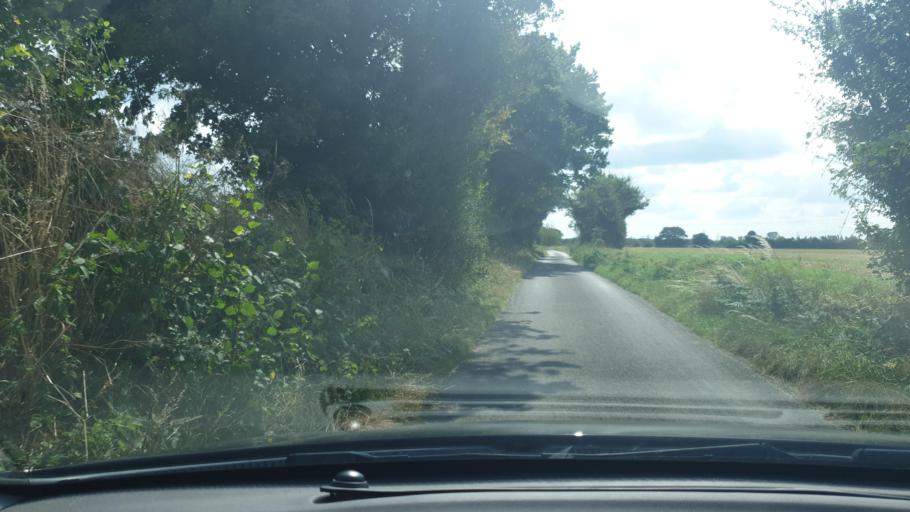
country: GB
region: England
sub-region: Essex
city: Manningtree
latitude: 51.9290
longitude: 1.0315
